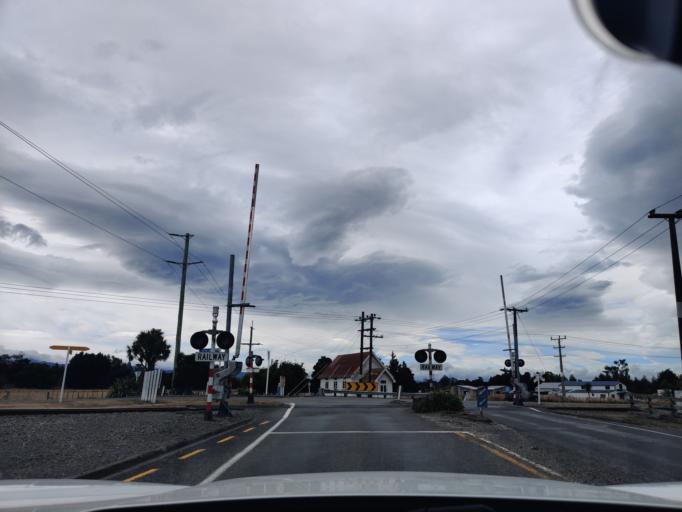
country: NZ
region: Wellington
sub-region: Masterton District
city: Masterton
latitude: -40.9583
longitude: 175.6140
